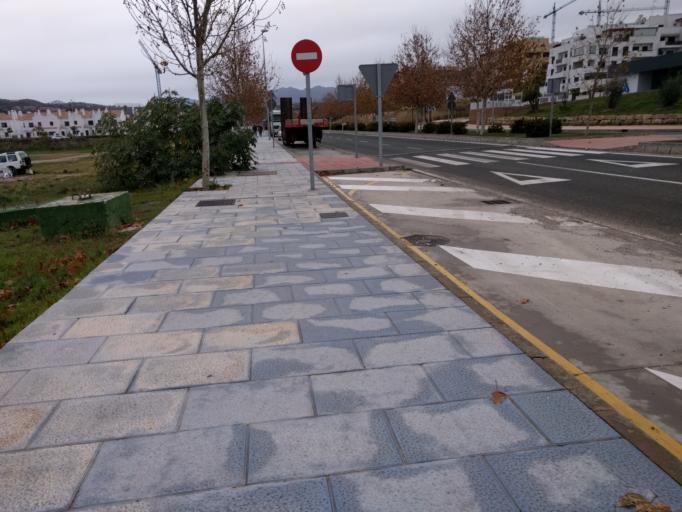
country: ES
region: Andalusia
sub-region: Provincia de Malaga
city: Fuengirola
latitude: 36.5066
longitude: -4.6828
